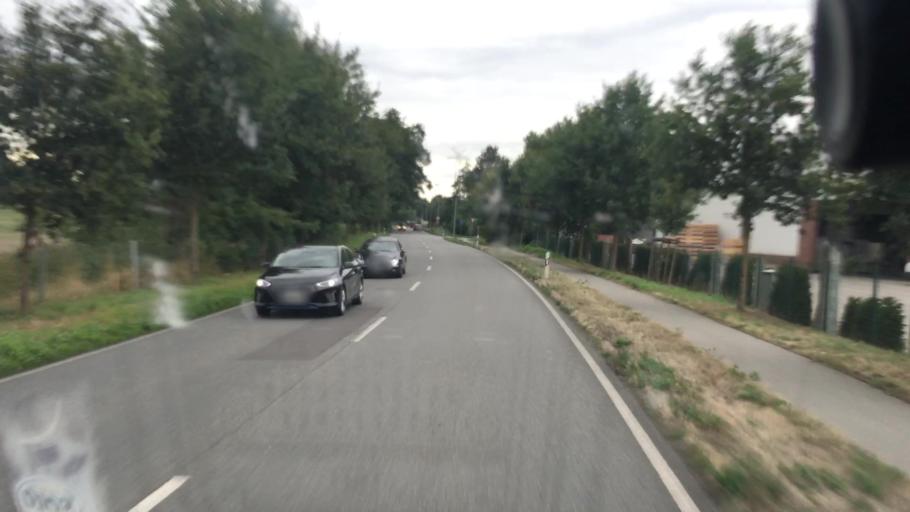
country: DE
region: Lower Saxony
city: Lohne
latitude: 52.6560
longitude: 8.1991
